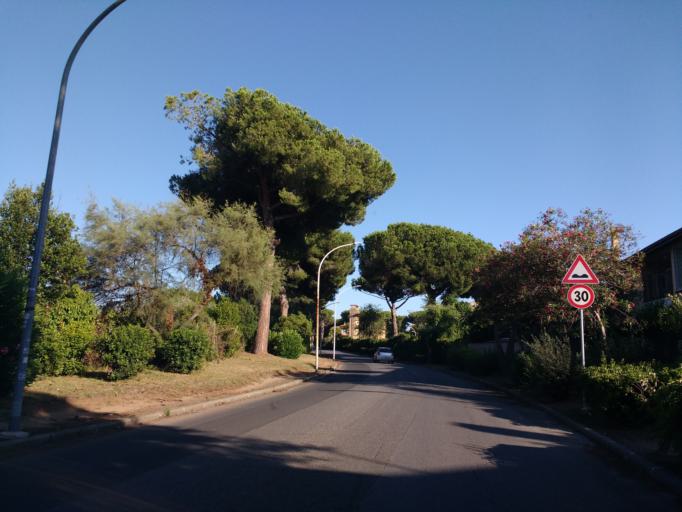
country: IT
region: Latium
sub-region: Citta metropolitana di Roma Capitale
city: Acilia-Castel Fusano-Ostia Antica
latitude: 41.7613
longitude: 12.3615
